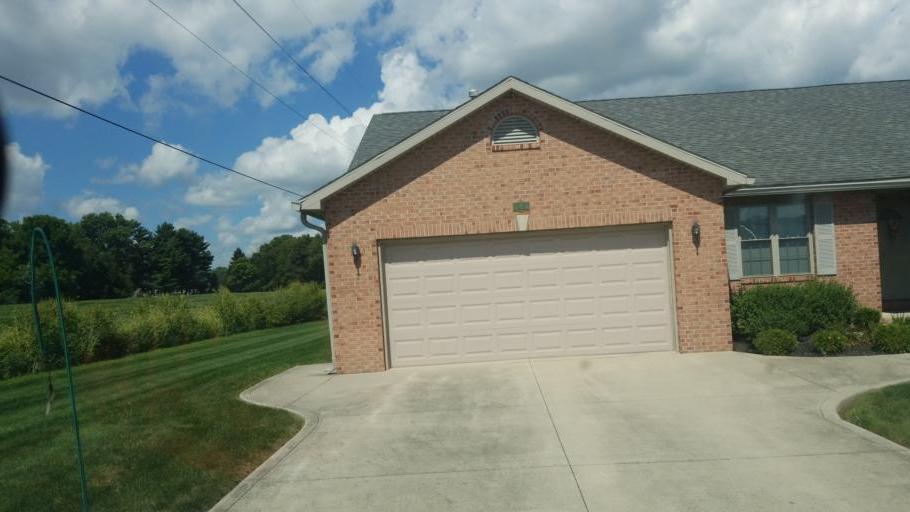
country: US
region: Ohio
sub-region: Marion County
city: Marion
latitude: 40.5665
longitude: -83.1073
